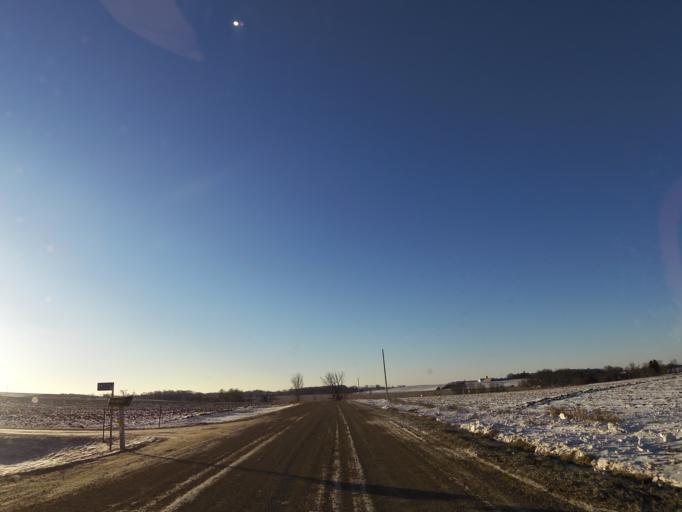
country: US
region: Minnesota
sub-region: Scott County
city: Jordan
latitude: 44.6662
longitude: -93.5419
